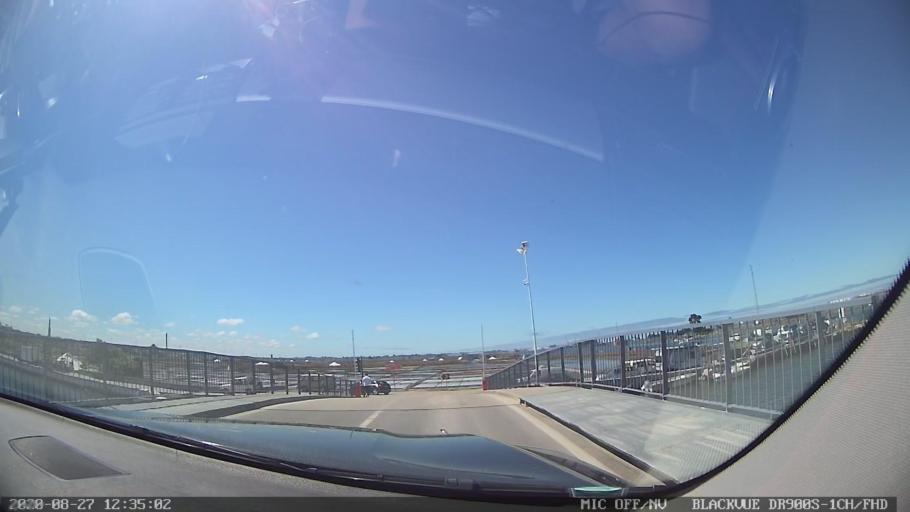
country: PT
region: Aveiro
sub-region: Aveiro
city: Aveiro
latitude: 40.6458
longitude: -8.6621
